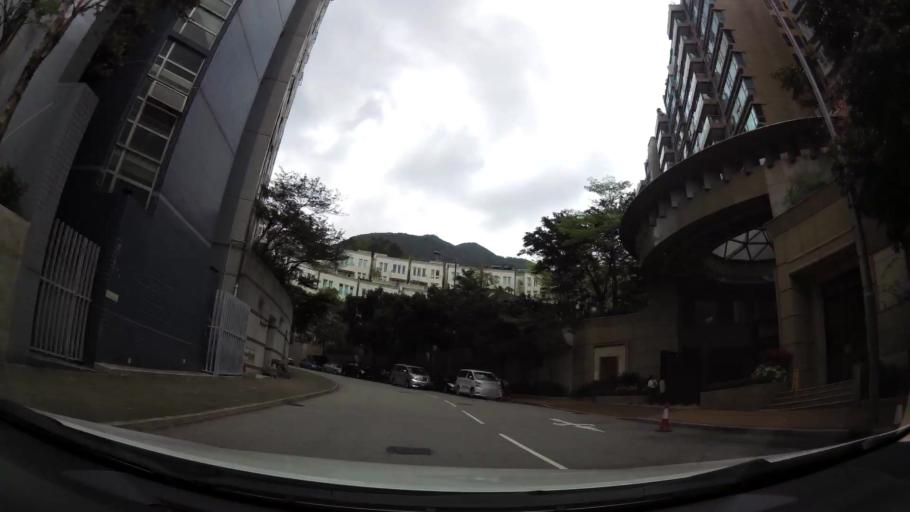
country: HK
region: Wong Tai Sin
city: Wong Tai Sin
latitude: 22.3400
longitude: 114.1717
